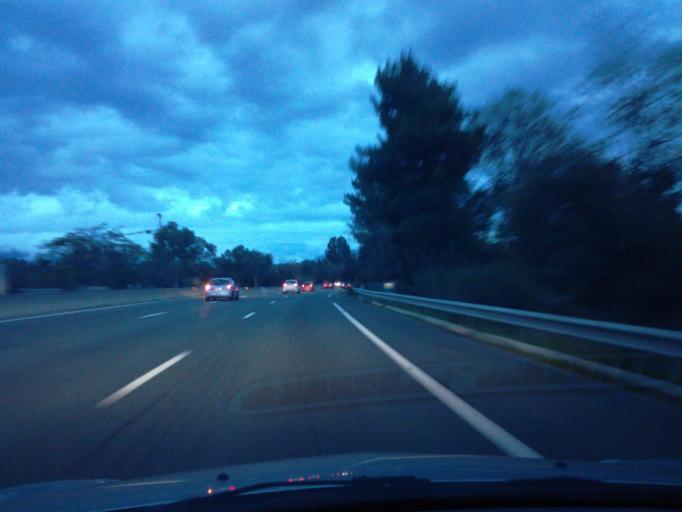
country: FR
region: Provence-Alpes-Cote d'Azur
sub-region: Departement des Alpes-Maritimes
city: Mandelieu-la-Napoule
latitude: 43.5537
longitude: 6.9449
